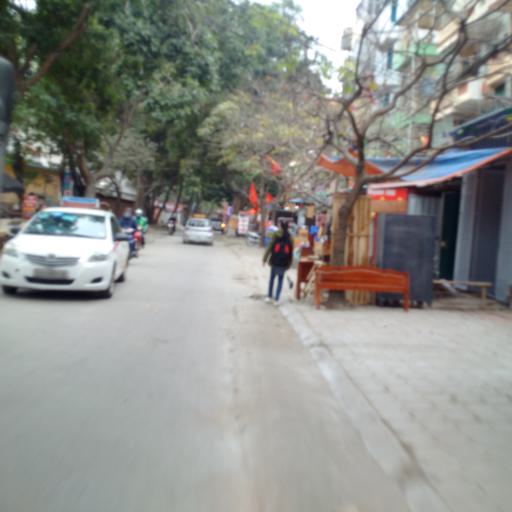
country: VN
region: Ha Noi
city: Tay Ho
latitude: 21.0694
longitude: 105.7783
